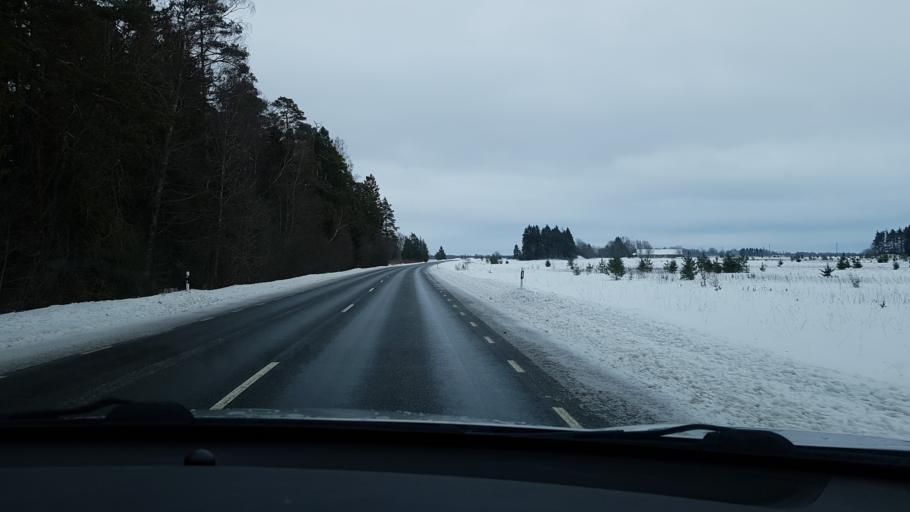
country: EE
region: Jaervamaa
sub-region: Jaerva-Jaani vald
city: Jarva-Jaani
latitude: 59.0937
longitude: 25.8261
